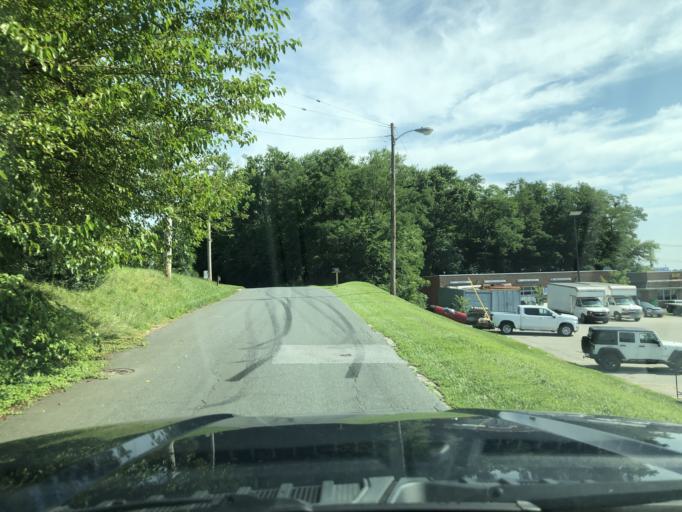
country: US
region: Maryland
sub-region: Carroll County
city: Eldersburg
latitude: 39.4064
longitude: -76.9515
